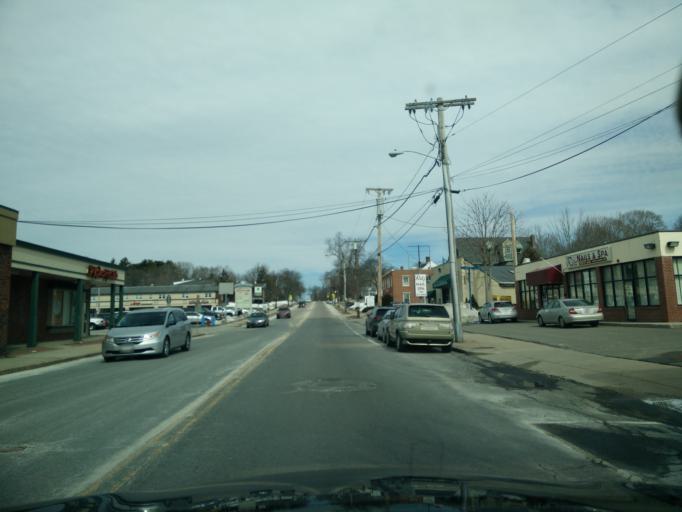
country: US
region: Massachusetts
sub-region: Norfolk County
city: Walpole
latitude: 42.1473
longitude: -71.2519
